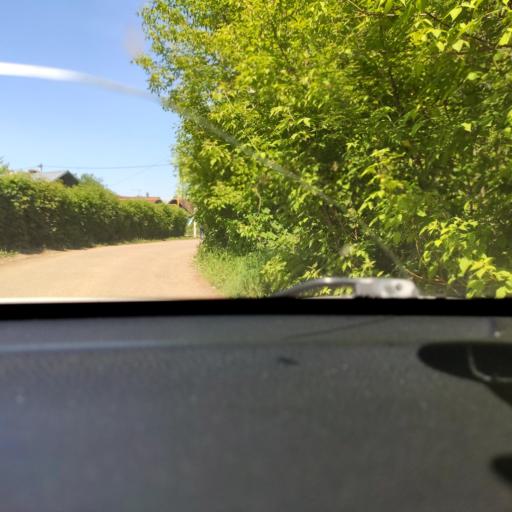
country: RU
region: Tatarstan
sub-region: Gorod Kazan'
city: Kazan
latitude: 55.8583
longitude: 49.1996
